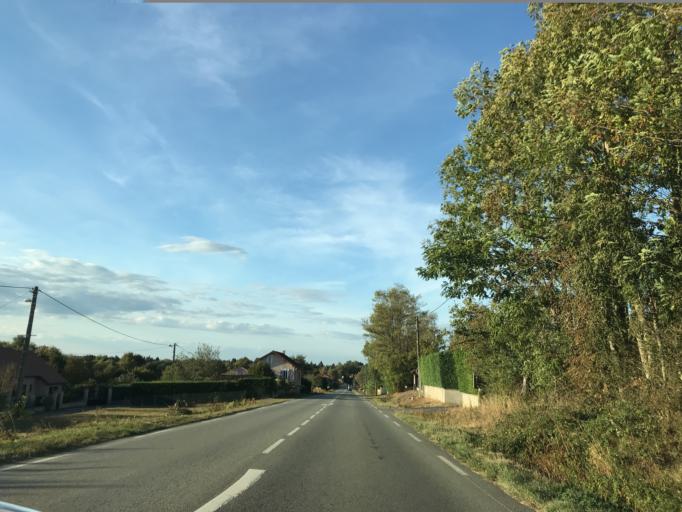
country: FR
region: Auvergne
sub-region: Departement du Puy-de-Dome
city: Paslieres
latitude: 45.9299
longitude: 3.4976
